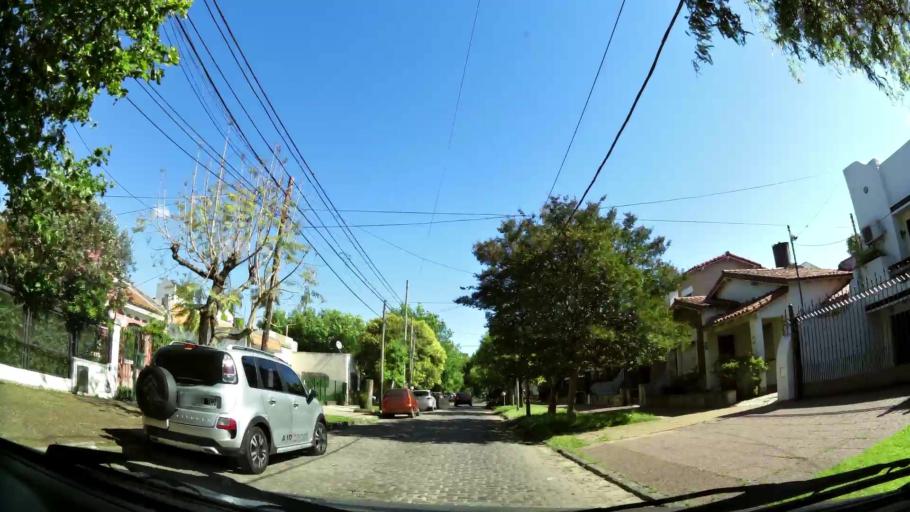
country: AR
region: Buenos Aires
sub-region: Partido de Lomas de Zamora
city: Lomas de Zamora
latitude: -34.7467
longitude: -58.4013
